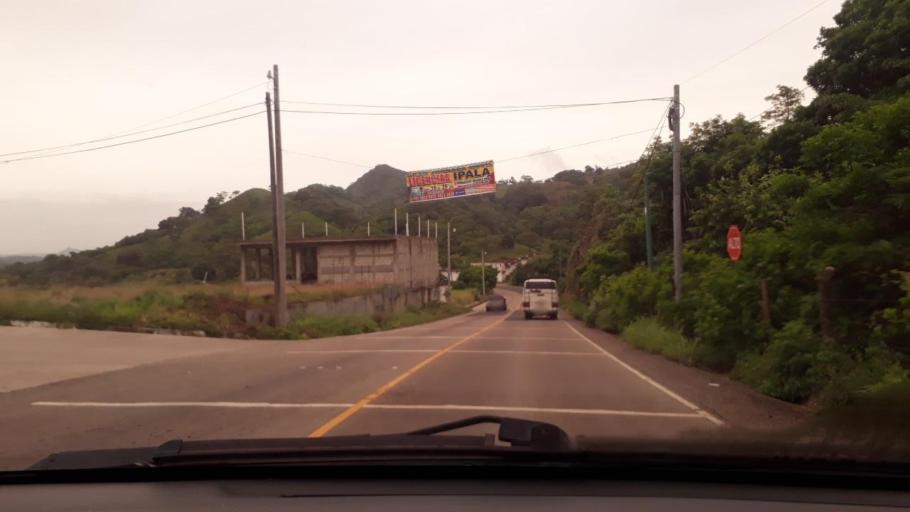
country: GT
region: Chiquimula
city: Concepcion Las Minas
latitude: 14.5313
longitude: -89.4630
